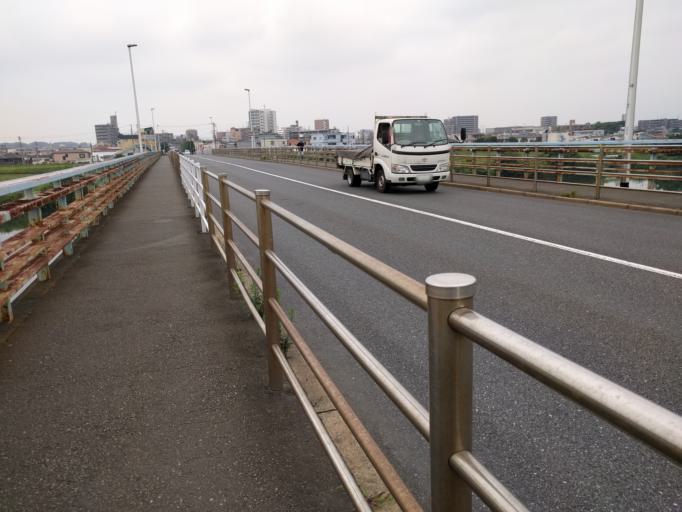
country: JP
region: Kanagawa
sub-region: Kawasaki-shi
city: Kawasaki
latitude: 35.5637
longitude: 139.6793
